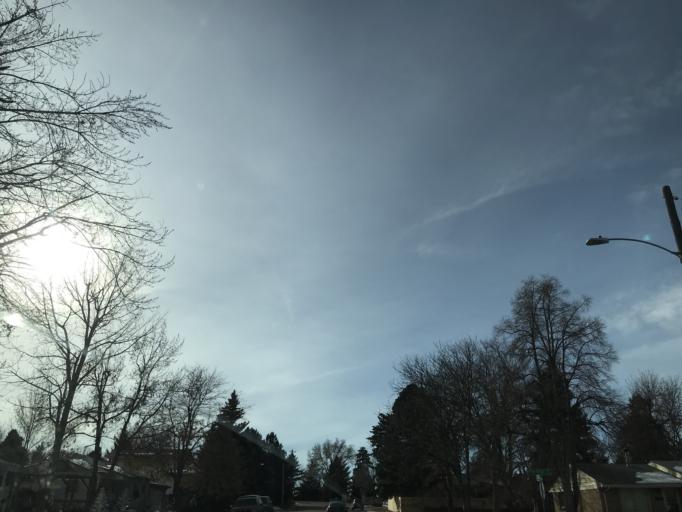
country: US
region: Colorado
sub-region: Arapahoe County
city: Littleton
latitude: 39.5997
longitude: -105.0117
